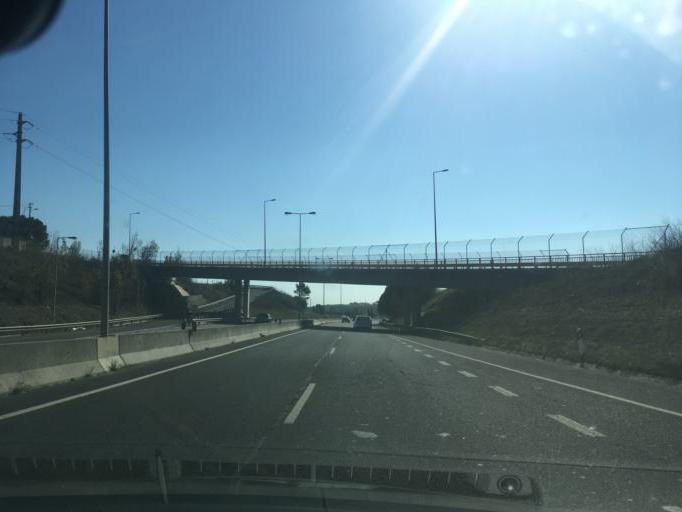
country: PT
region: Lisbon
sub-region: Oeiras
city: Porto Salvo
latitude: 38.7323
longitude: -9.2974
